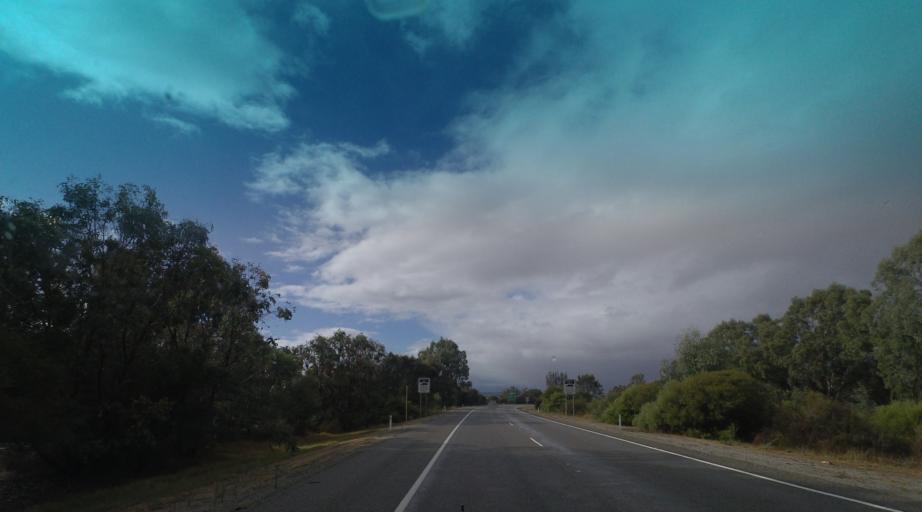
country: AU
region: Western Australia
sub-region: Serpentine-Jarrahdale
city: Oakford
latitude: -32.2035
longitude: 115.9676
